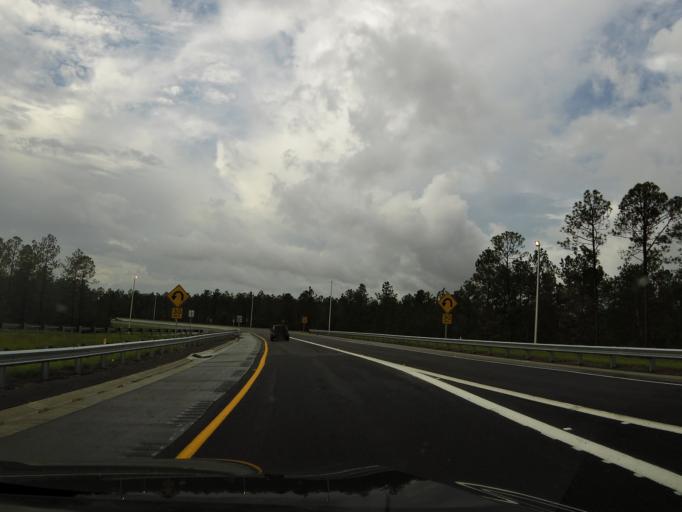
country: US
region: Florida
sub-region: Duval County
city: Baldwin
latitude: 30.3137
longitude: -81.8786
